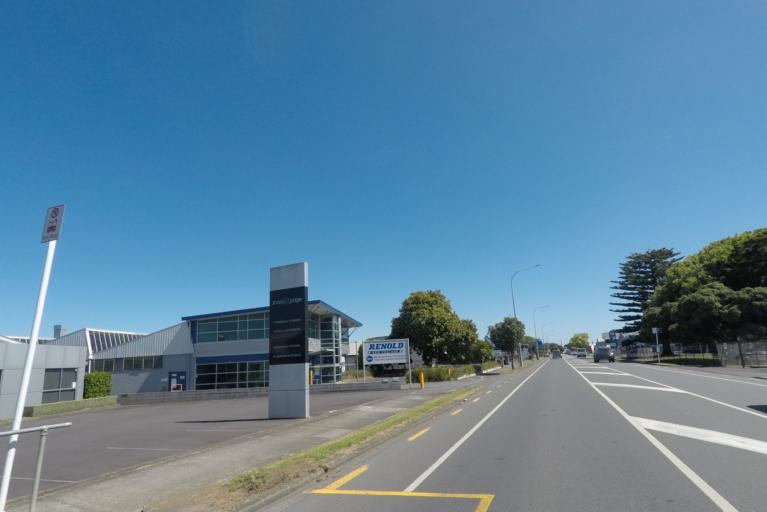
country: NZ
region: Auckland
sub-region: Auckland
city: Rosebank
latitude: -36.8756
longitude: 174.6698
